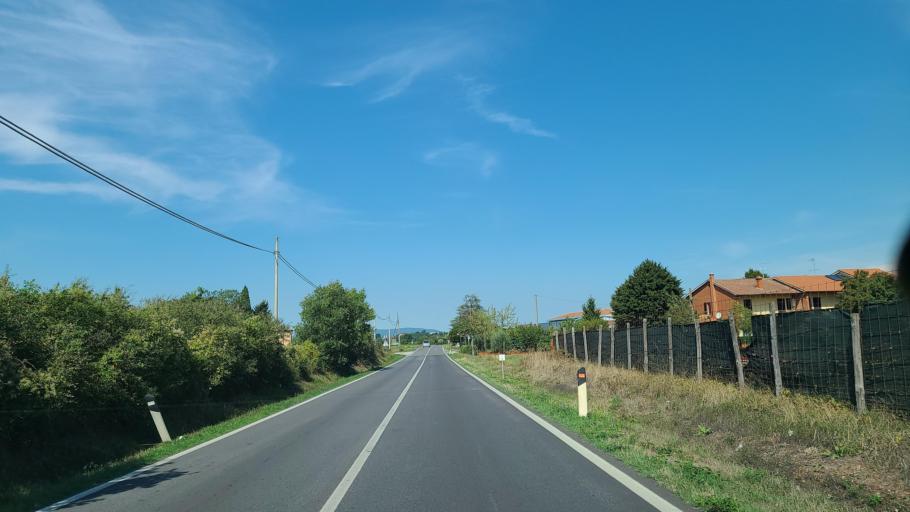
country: IT
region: Tuscany
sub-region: Provincia di Siena
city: Staggia
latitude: 43.3957
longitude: 11.1818
